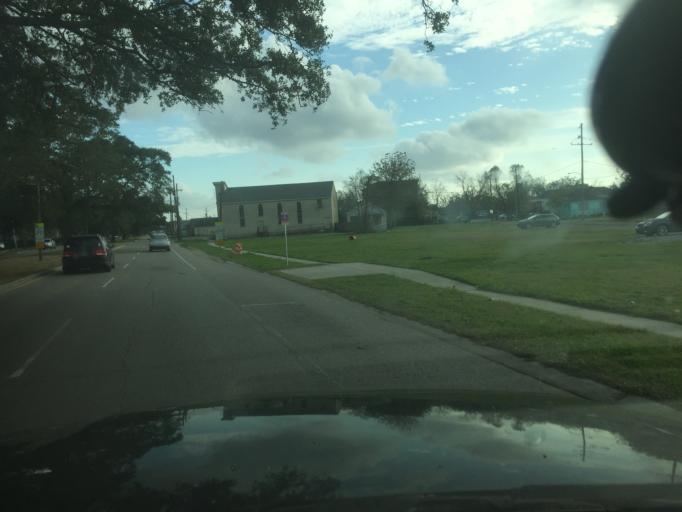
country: US
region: Louisiana
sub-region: Orleans Parish
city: New Orleans
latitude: 29.9986
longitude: -90.0806
